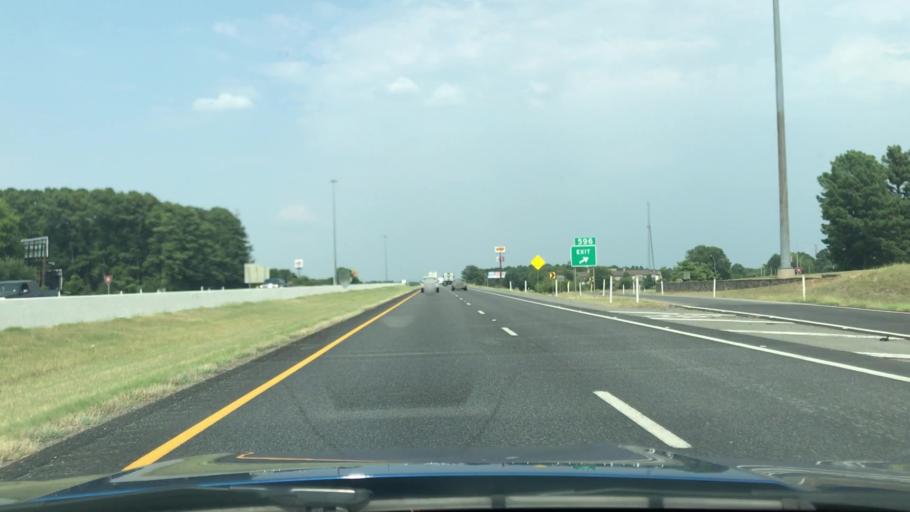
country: US
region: Texas
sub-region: Gregg County
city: Longview
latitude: 32.4486
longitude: -94.7131
